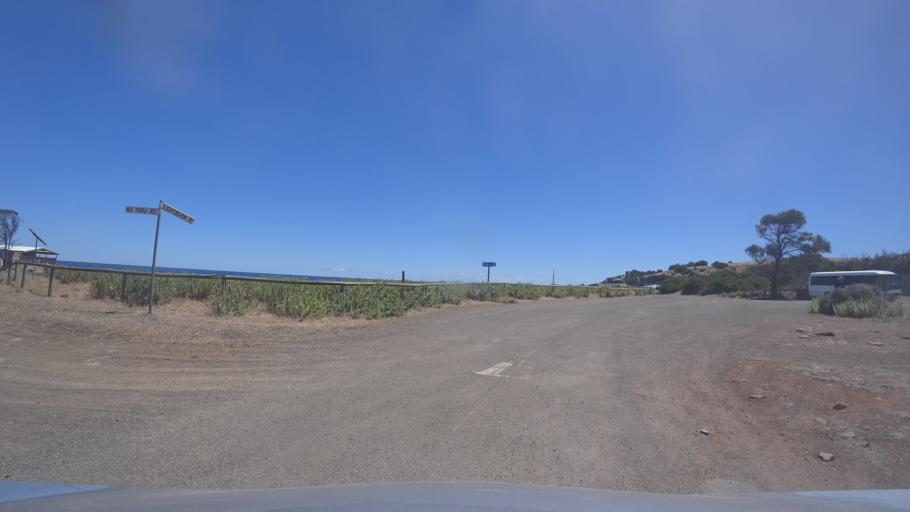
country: AU
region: South Australia
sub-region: Kangaroo Island
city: Kingscote
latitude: -35.6251
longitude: 137.2061
